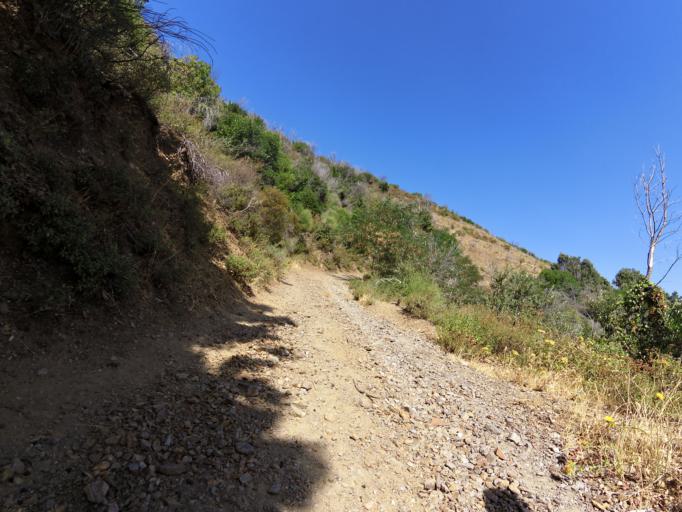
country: IT
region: Calabria
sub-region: Provincia di Reggio Calabria
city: Bivongi
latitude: 38.4997
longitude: 16.4516
